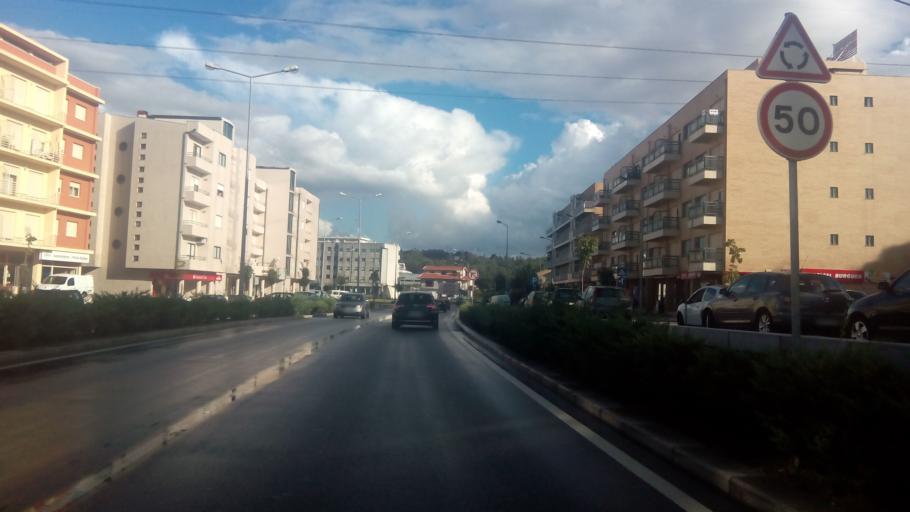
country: PT
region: Porto
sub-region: Valongo
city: Campo
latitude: 41.1833
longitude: -8.4453
